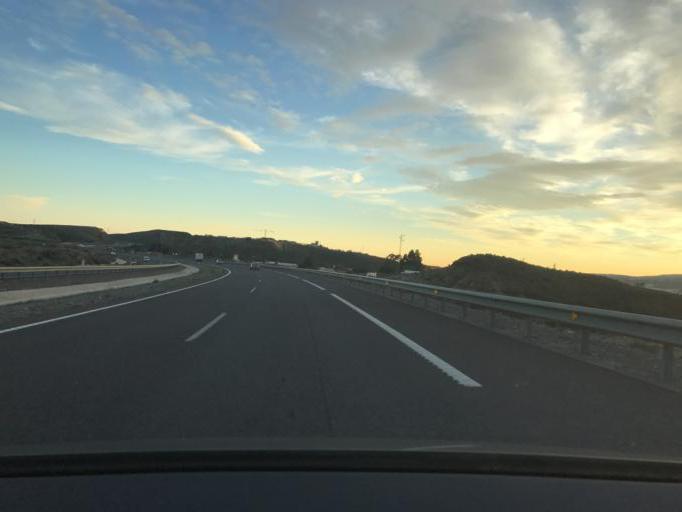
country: ES
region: Andalusia
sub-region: Provincia de Almeria
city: Pechina
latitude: 36.9104
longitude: -2.4202
